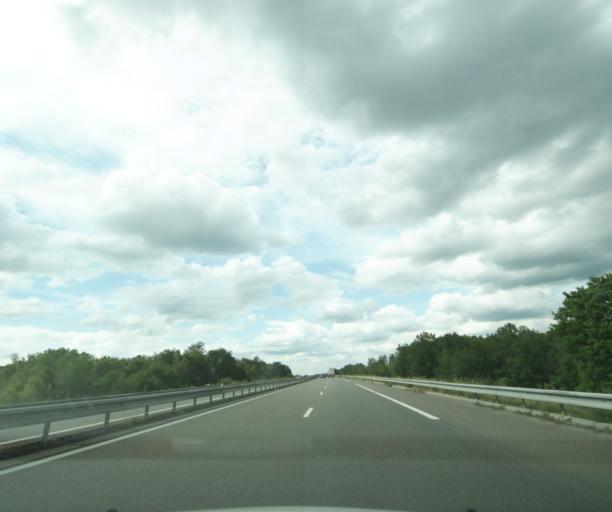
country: FR
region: Centre
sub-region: Departement du Loir-et-Cher
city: Salbris
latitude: 47.3805
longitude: 2.0519
